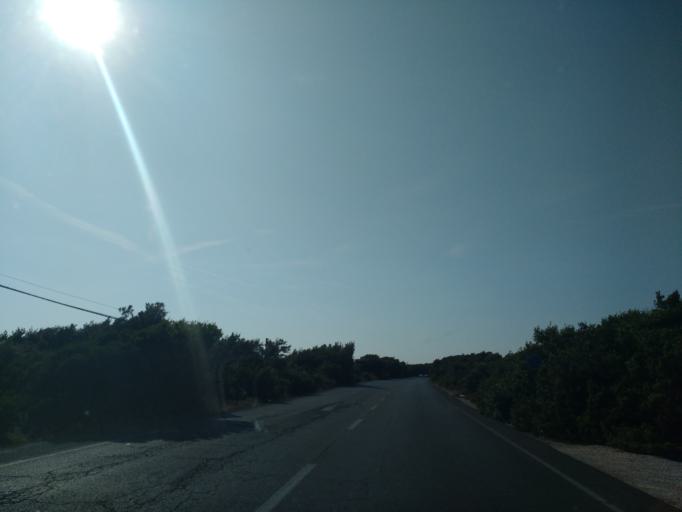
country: IT
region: Latium
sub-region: Citta metropolitana di Roma Capitale
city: Acilia-Castel Fusano-Ostia Antica
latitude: 41.6896
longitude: 12.3702
